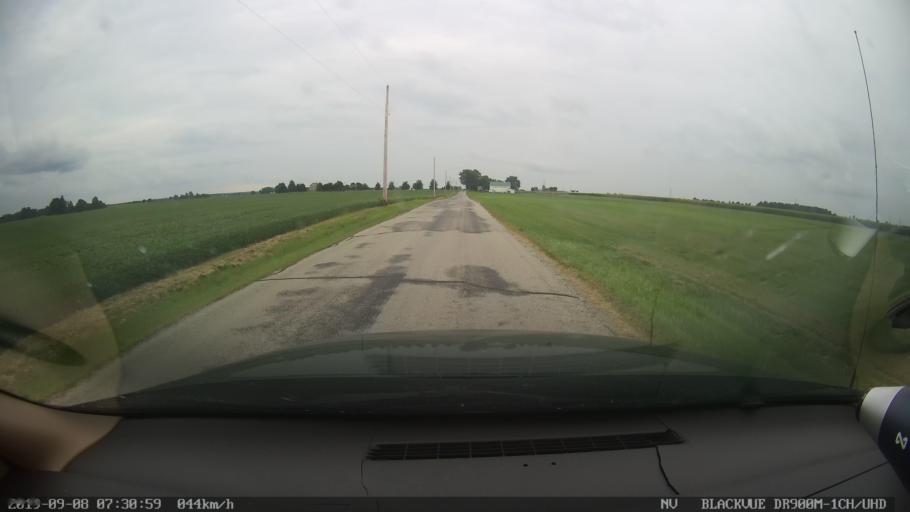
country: US
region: Ohio
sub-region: Richland County
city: Shelby
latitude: 40.8721
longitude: -82.6957
